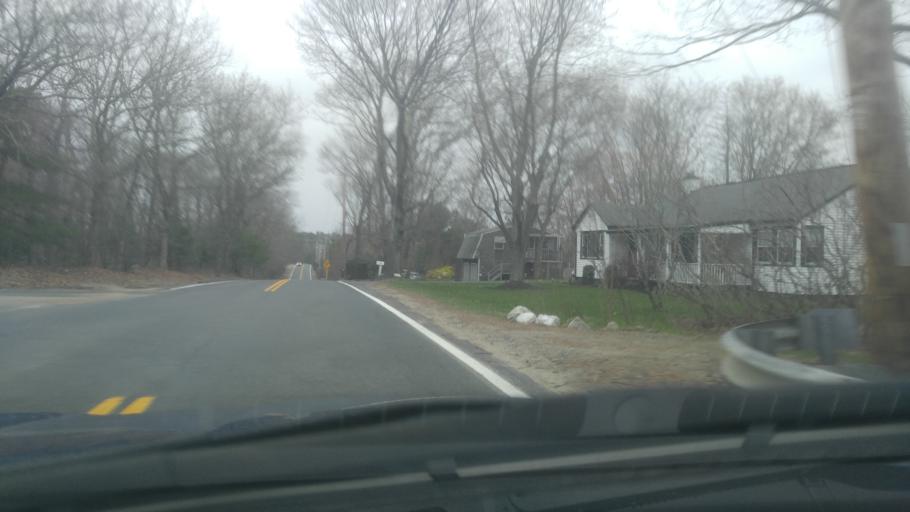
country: US
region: Rhode Island
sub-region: Kent County
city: West Warwick
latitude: 41.6548
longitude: -71.5504
